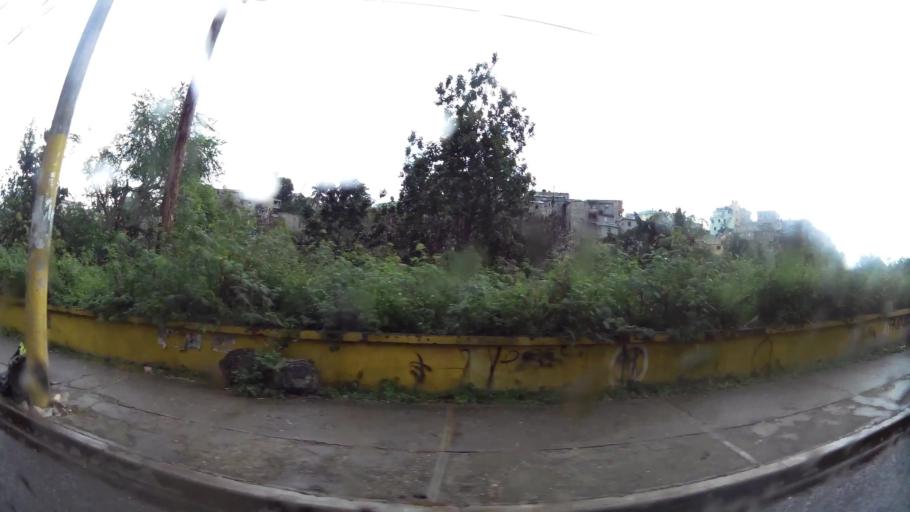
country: DO
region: Nacional
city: La Agustina
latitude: 18.5017
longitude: -69.9322
